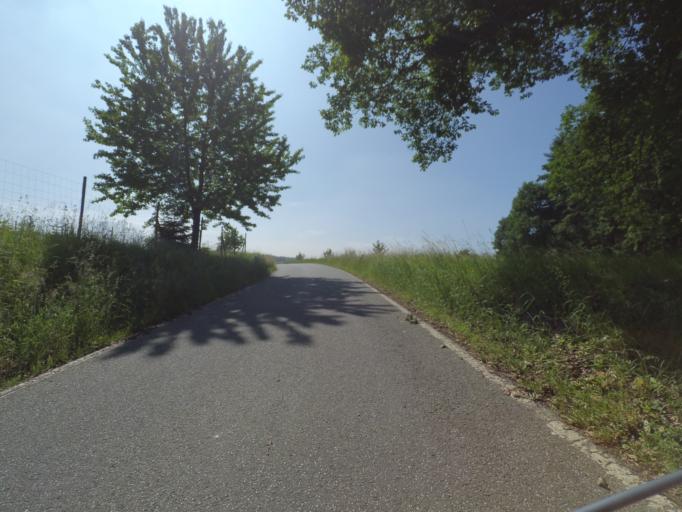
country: DE
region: Rheinland-Pfalz
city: Brodenbach
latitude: 50.2172
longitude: 7.4583
